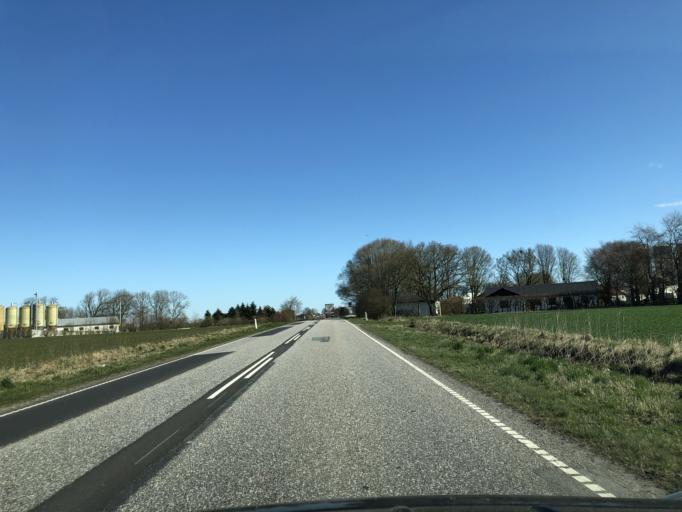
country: DK
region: North Denmark
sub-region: Rebild Kommune
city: Stovring
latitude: 56.8544
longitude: 9.8256
